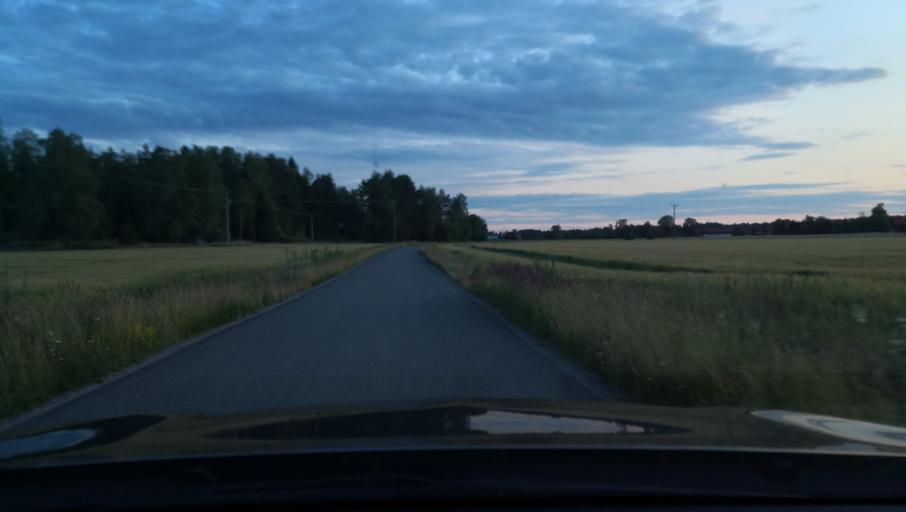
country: SE
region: Uppsala
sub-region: Osthammars Kommun
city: Bjorklinge
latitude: 60.0372
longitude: 17.4939
